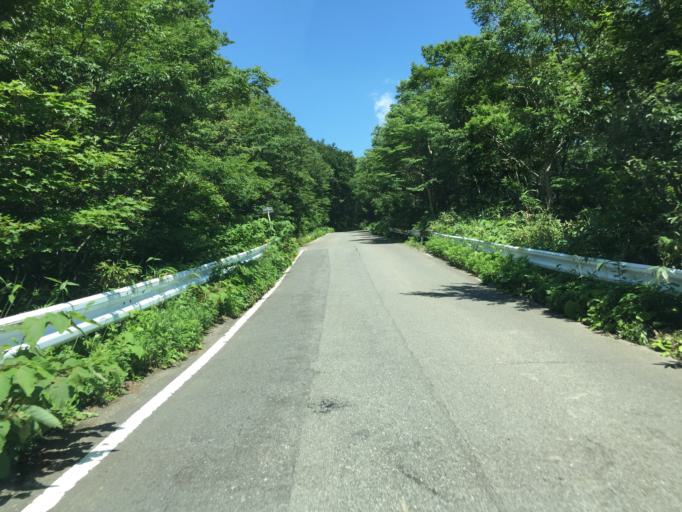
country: JP
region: Fukushima
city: Nihommatsu
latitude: 37.6600
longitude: 140.2860
